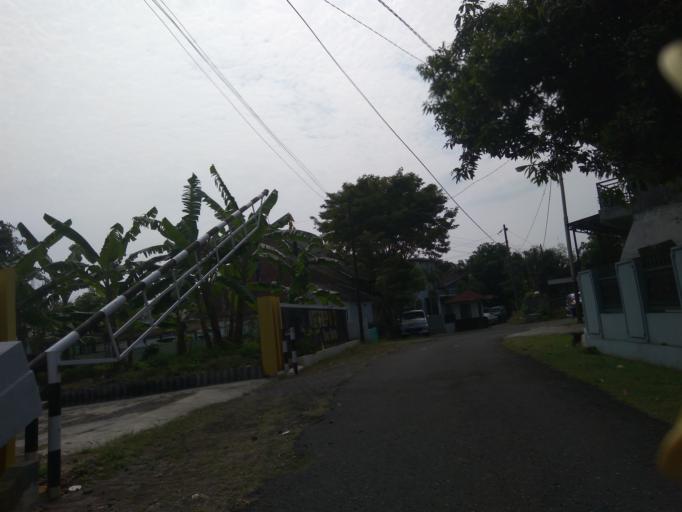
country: ID
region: Central Java
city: Semarang
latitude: -7.0454
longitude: 110.4169
